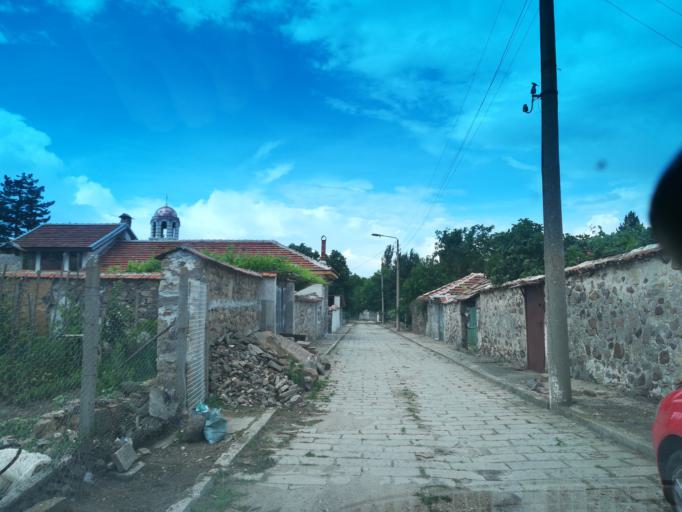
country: BG
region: Khaskovo
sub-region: Obshtina Mineralni Bani
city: Mineralni Bani
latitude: 41.9928
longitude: 25.2330
